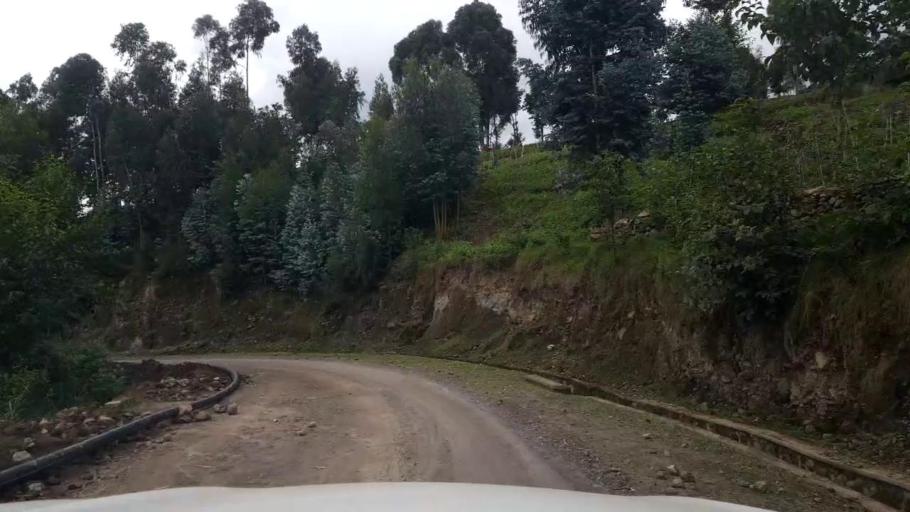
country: RW
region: Northern Province
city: Musanze
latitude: -1.5342
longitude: 29.5331
